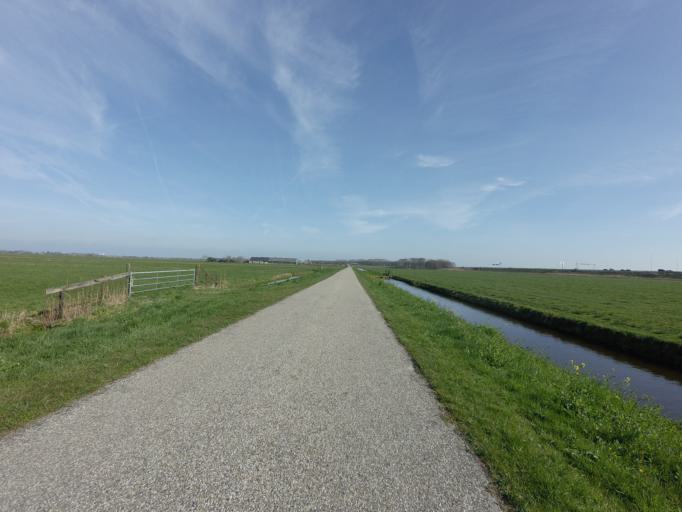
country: NL
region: South Holland
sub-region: Bodegraven-Reeuwijk
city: Bodegraven
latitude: 52.0679
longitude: 4.7994
